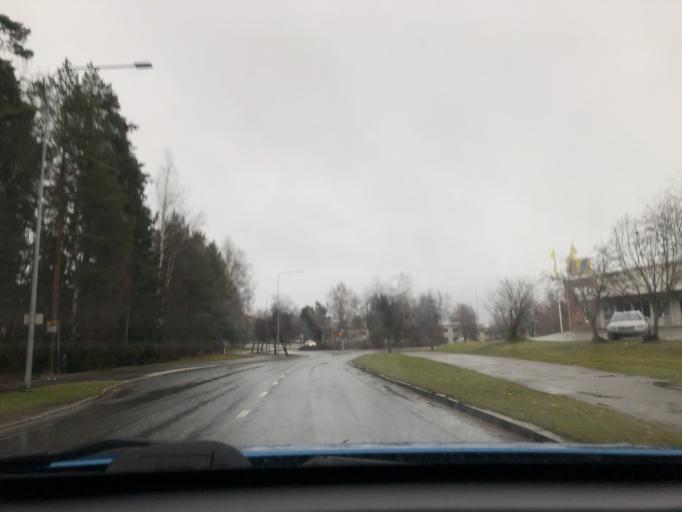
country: FI
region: Pirkanmaa
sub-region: Tampere
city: Kangasala
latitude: 61.4698
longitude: 24.0381
